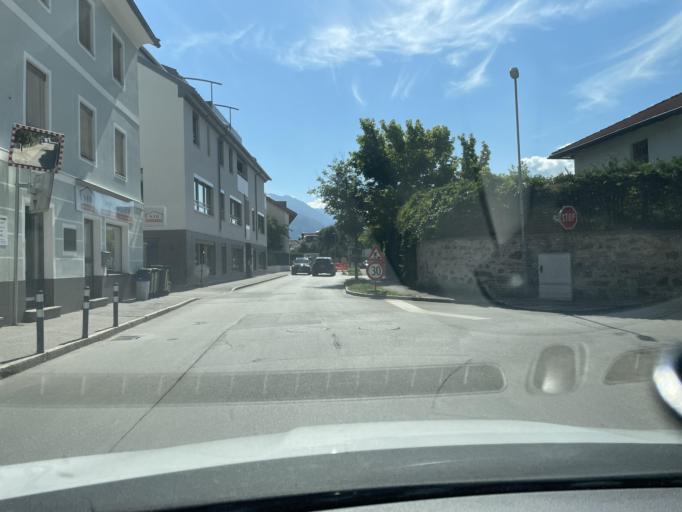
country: AT
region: Tyrol
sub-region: Politischer Bezirk Lienz
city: Lienz
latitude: 46.8327
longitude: 12.7696
